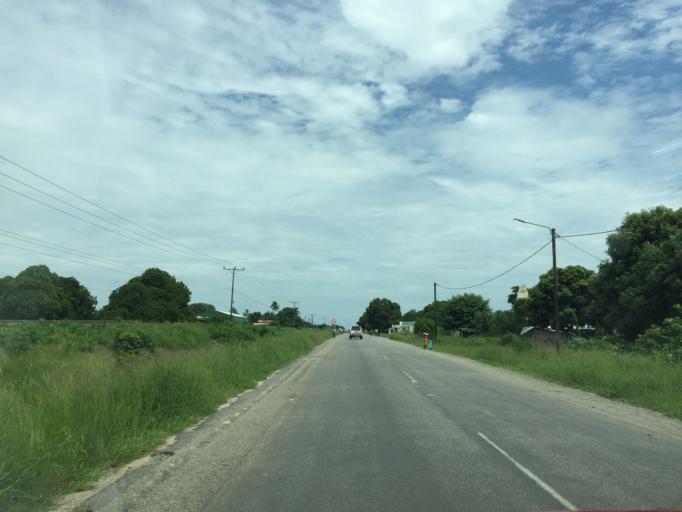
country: MZ
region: Zambezia
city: Quelimane
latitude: -17.5849
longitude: 36.8093
